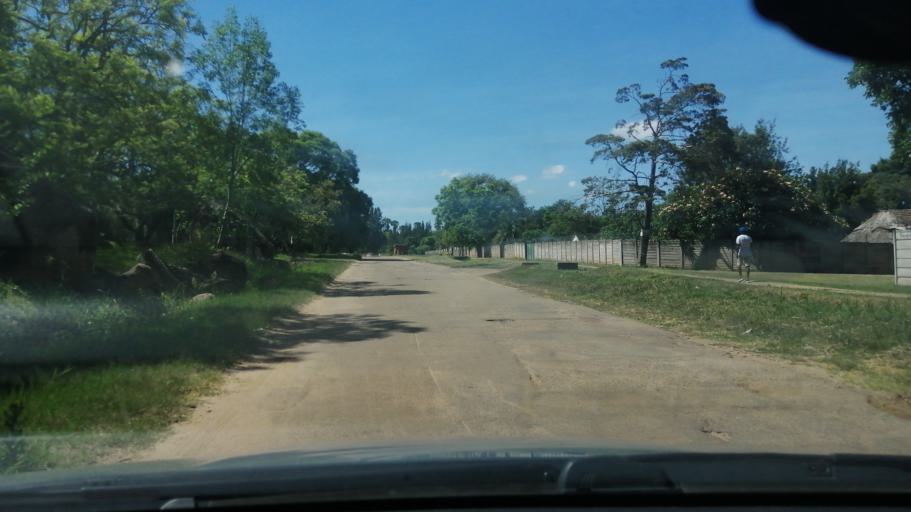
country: ZW
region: Harare
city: Harare
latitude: -17.8147
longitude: 31.1287
